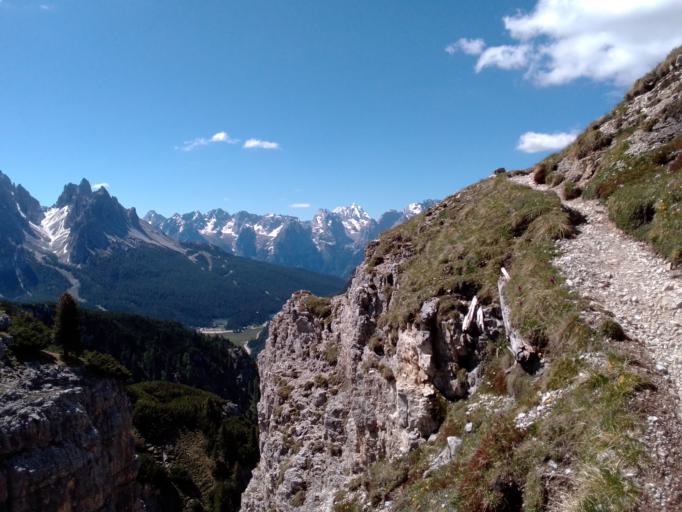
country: IT
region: Trentino-Alto Adige
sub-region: Bolzano
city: Dobbiaco
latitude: 46.6142
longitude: 12.2445
